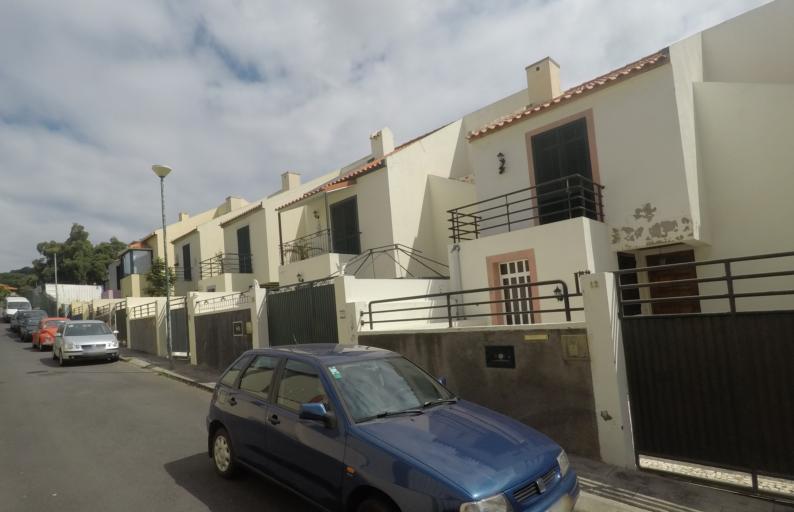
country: PT
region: Madeira
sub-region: Funchal
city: Funchal
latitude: 32.6457
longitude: -16.9323
